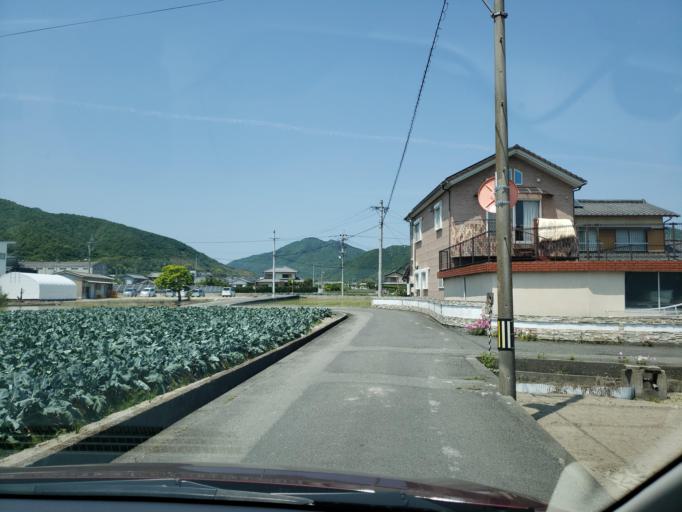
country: JP
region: Tokushima
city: Kamojimacho-jogejima
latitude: 34.0980
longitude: 134.2690
